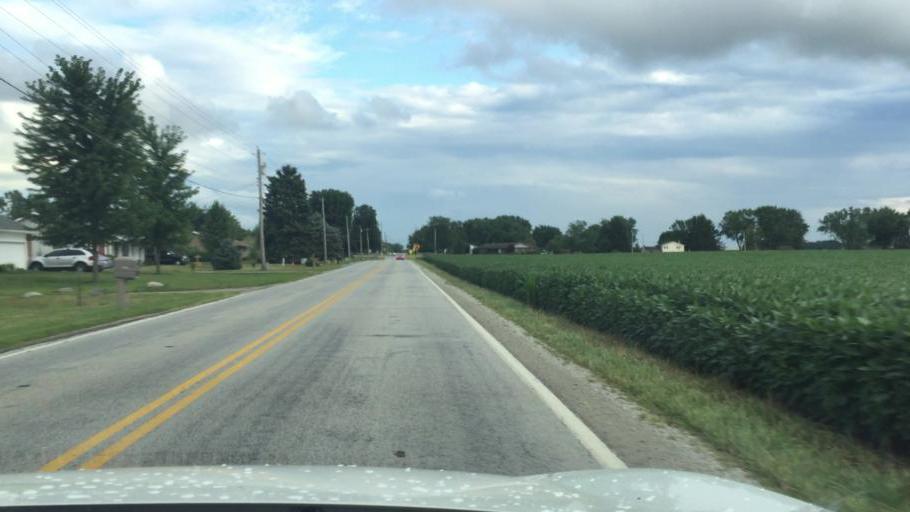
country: US
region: Ohio
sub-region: Clark County
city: Lisbon
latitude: 39.9449
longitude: -83.6819
